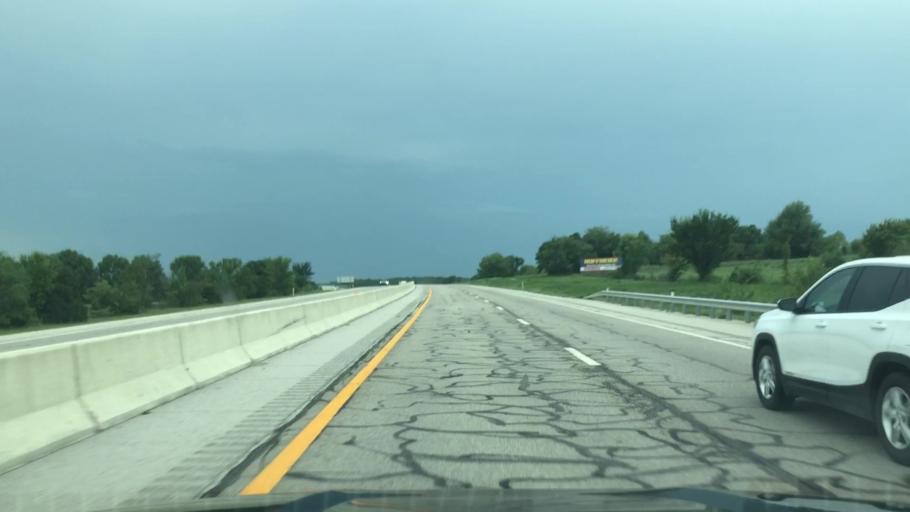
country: US
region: Oklahoma
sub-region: Rogers County
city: Chelsea
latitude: 36.4465
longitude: -95.3727
